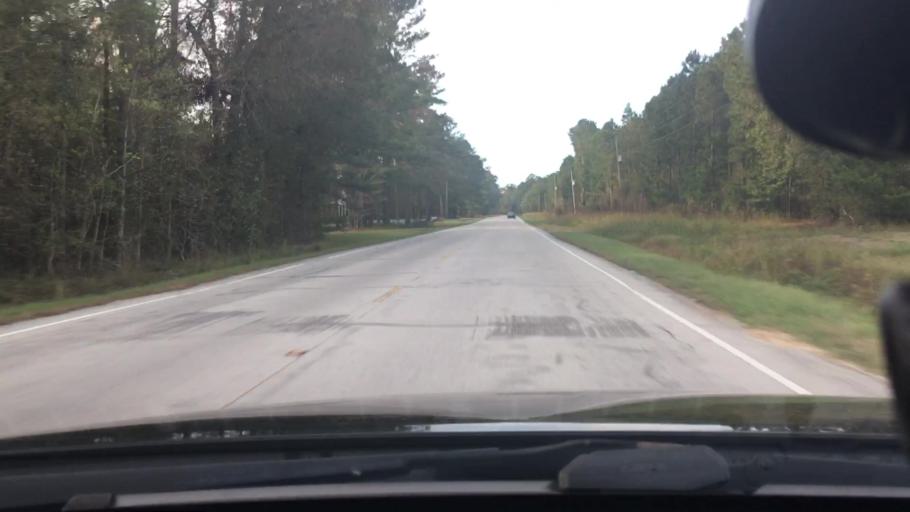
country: US
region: North Carolina
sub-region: Craven County
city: Vanceboro
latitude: 35.4037
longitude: -77.2405
